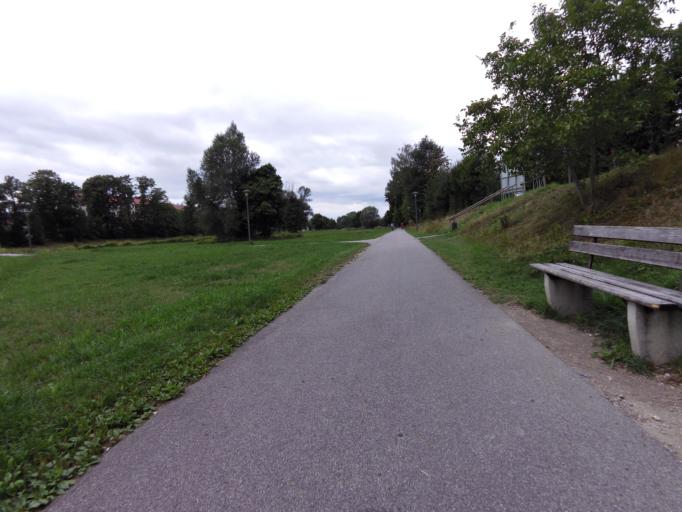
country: DE
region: Bavaria
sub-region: Lower Bavaria
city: Landshut
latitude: 48.5485
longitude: 12.1539
